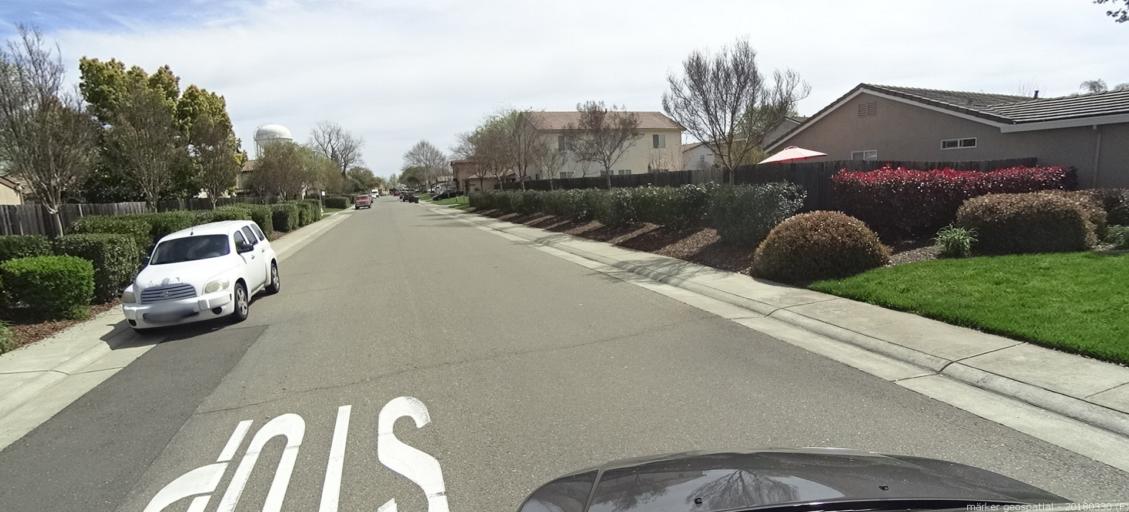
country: US
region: California
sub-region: Sacramento County
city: Rancho Cordova
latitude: 38.5451
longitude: -121.2830
